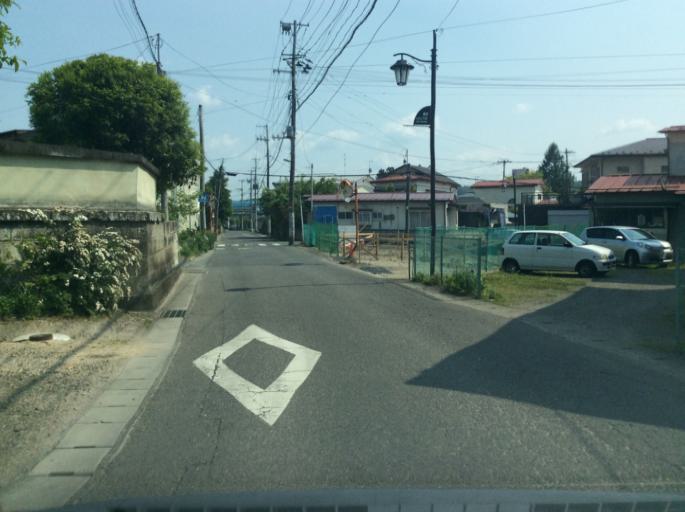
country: JP
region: Fukushima
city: Sukagawa
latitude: 37.1270
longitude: 140.2228
